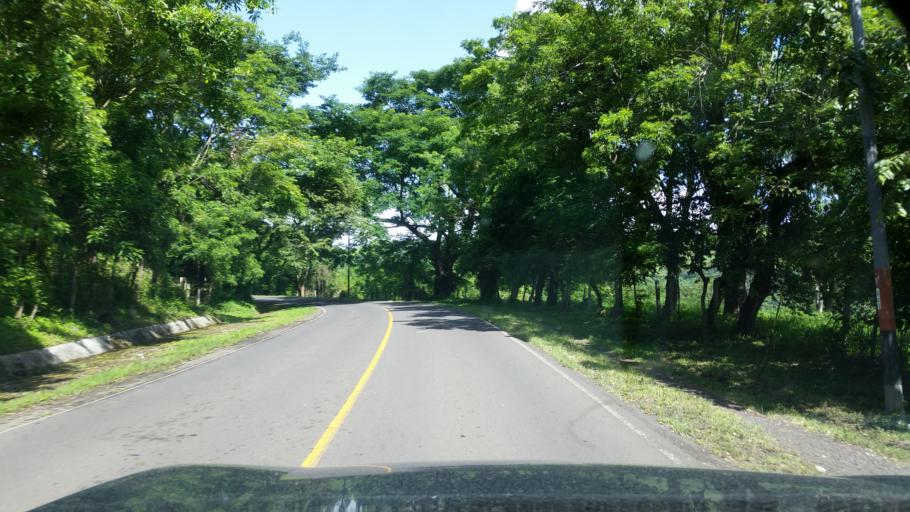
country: NI
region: Matagalpa
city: San Ramon
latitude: 13.0061
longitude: -85.7974
